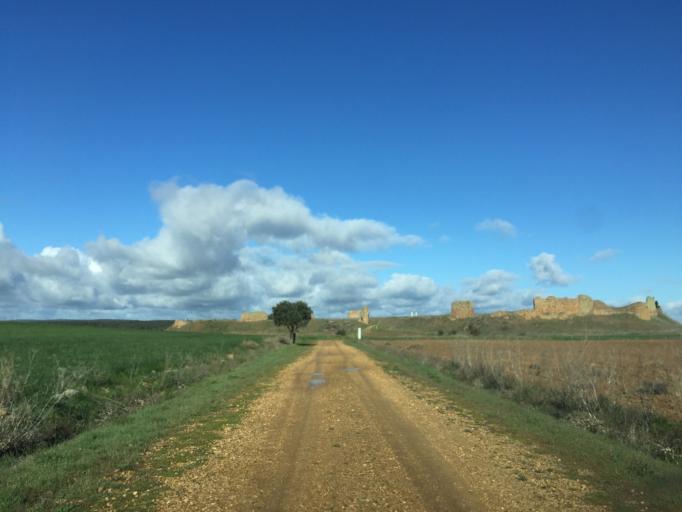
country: ES
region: Castille and Leon
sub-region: Provincia de Zamora
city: San Cebrian de Castro
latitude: 41.7203
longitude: -5.7898
